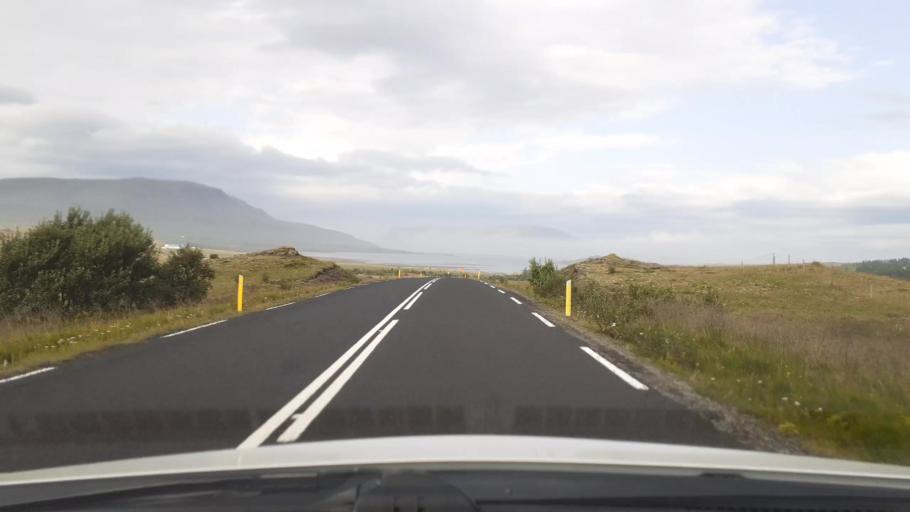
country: IS
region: Capital Region
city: Mosfellsbaer
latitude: 64.3424
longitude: -21.5942
